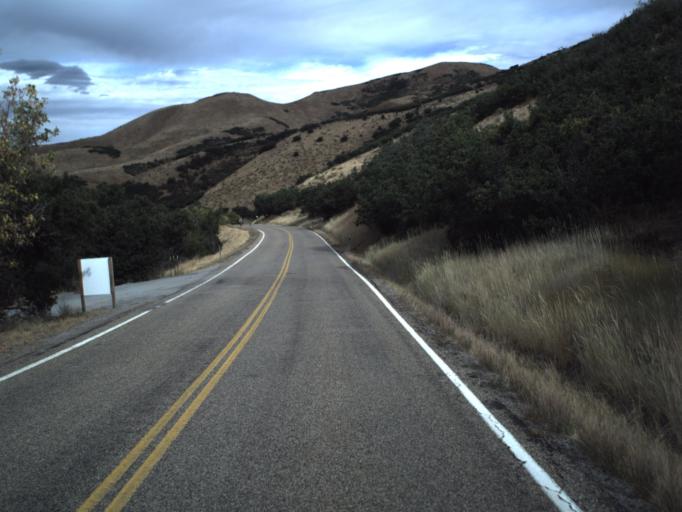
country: US
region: Utah
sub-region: Morgan County
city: Morgan
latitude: 40.9285
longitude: -111.6156
